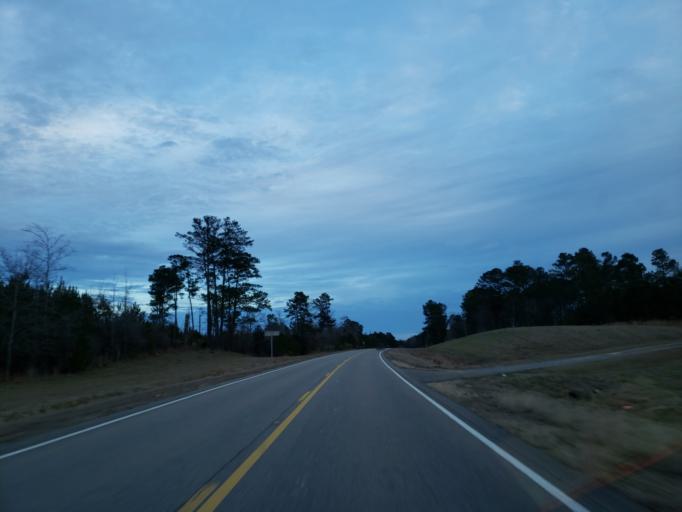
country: US
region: Mississippi
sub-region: Kemper County
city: De Kalb
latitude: 32.8309
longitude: -88.3663
